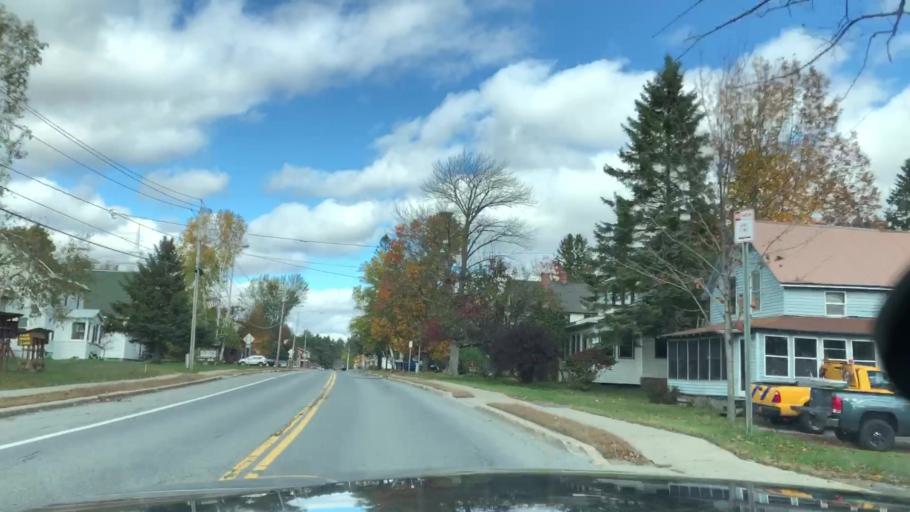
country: US
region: New York
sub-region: Hamilton County
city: Lake Pleasant
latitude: 43.7797
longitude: -74.2649
